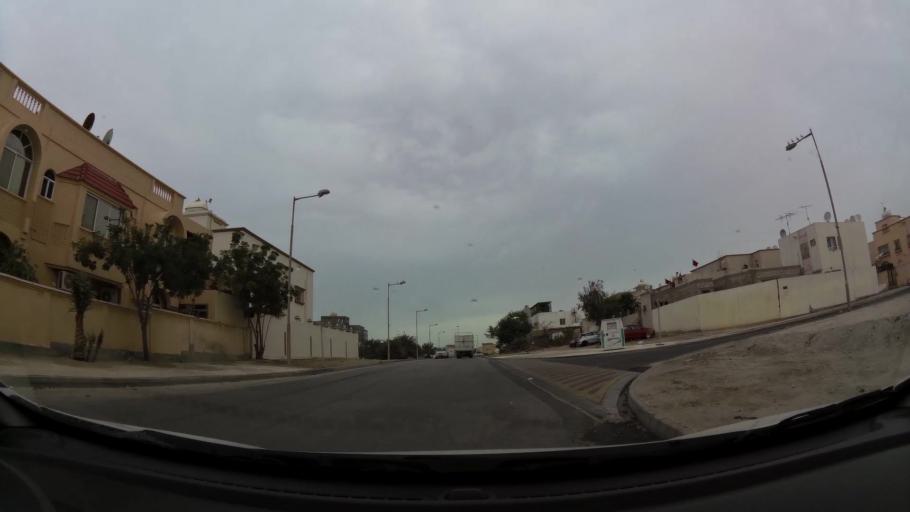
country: BH
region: Central Governorate
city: Madinat Hamad
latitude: 26.1011
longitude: 50.5018
